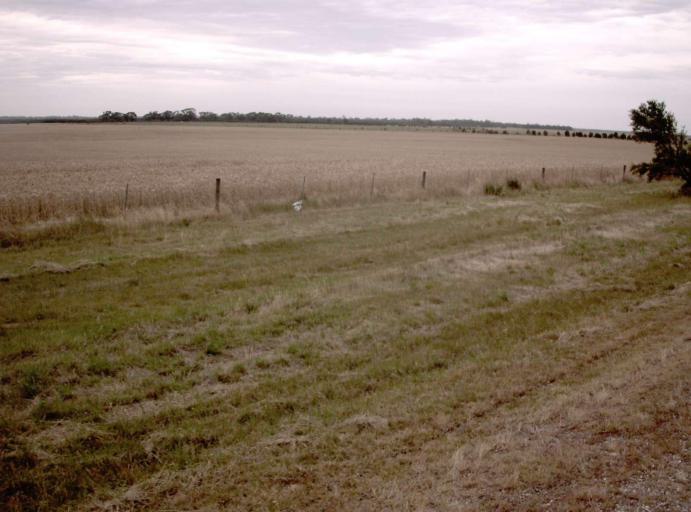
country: AU
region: Victoria
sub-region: Wellington
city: Sale
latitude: -38.2005
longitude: 147.3115
